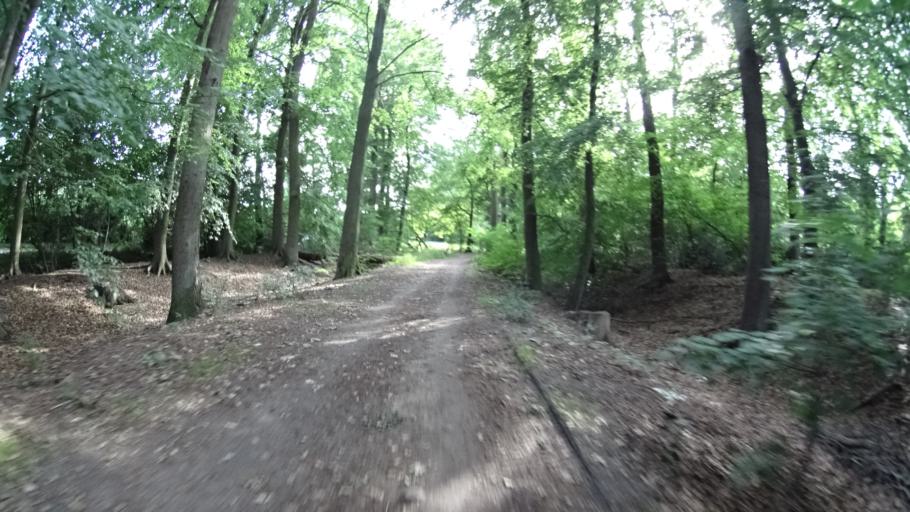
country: DE
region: Lower Saxony
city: Vogelsen
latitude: 53.2737
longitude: 10.3611
